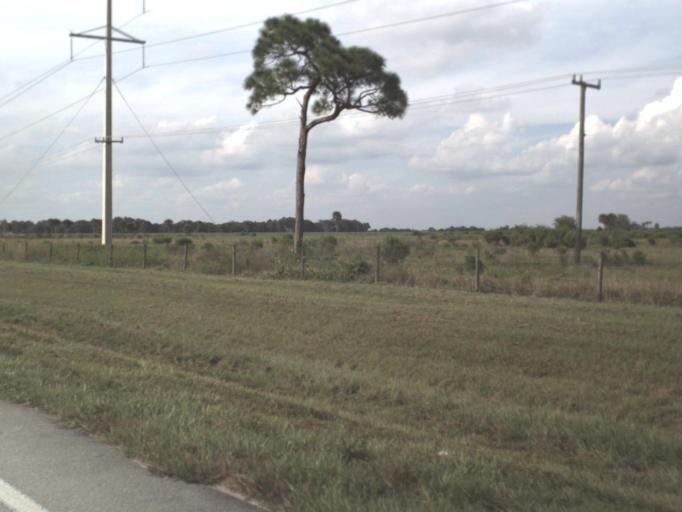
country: US
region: Florida
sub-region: Okeechobee County
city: Taylor Creek
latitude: 27.1968
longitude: -80.7344
